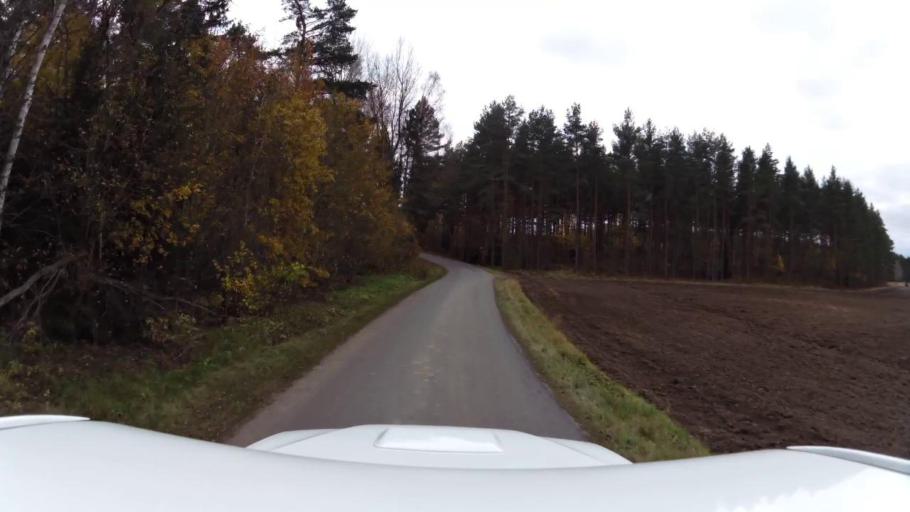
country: SE
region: OEstergoetland
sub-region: Linkopings Kommun
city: Linghem
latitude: 58.4032
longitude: 15.8449
